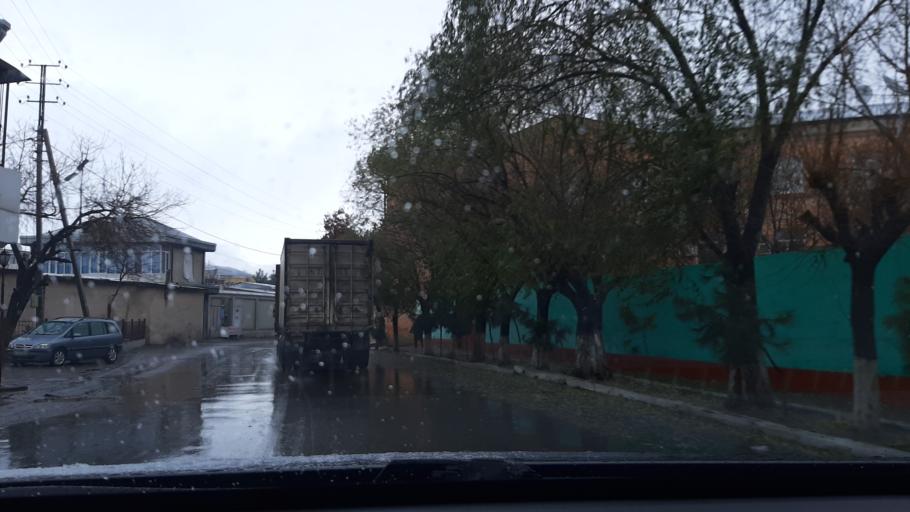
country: TJ
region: Viloyati Sughd
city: Khujand
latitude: 40.2722
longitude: 69.6384
